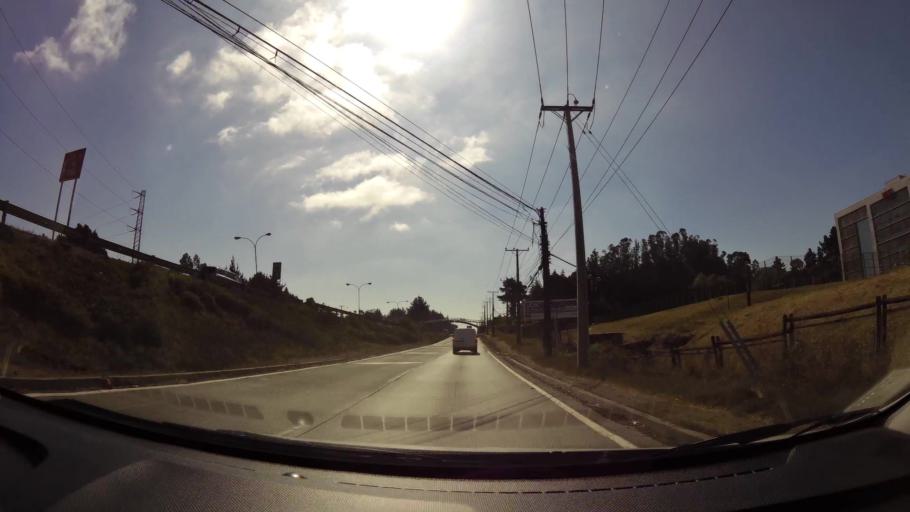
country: CL
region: Biobio
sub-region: Provincia de Concepcion
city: Concepcion
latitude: -36.7991
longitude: -73.0582
